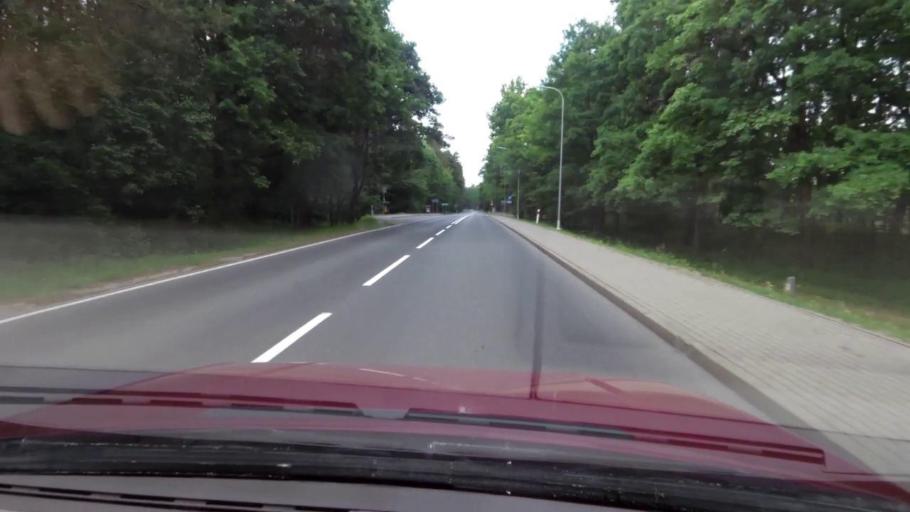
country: PL
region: Pomeranian Voivodeship
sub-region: Powiat bytowski
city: Trzebielino
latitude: 54.2511
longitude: 17.1023
